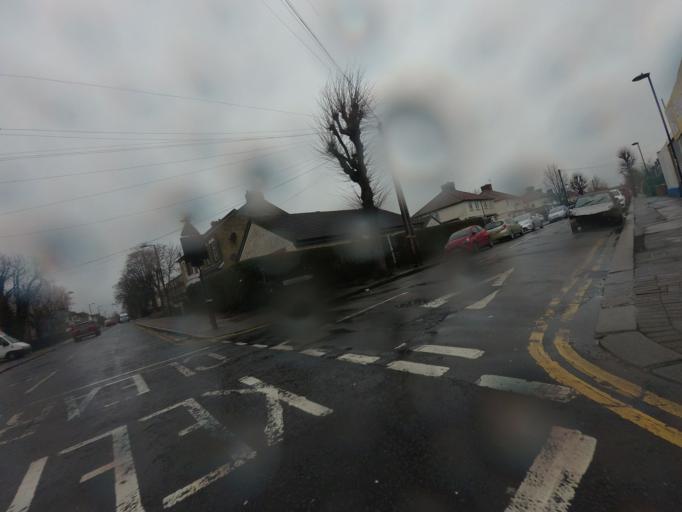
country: GB
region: England
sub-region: Hertfordshire
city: Waltham Cross
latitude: 51.6713
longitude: -0.0302
